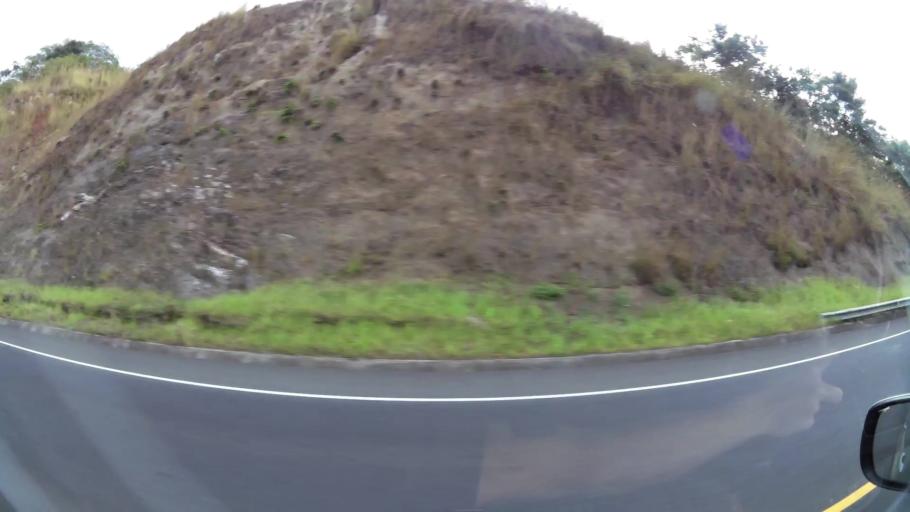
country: CR
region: Alajuela
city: Atenas
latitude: 9.9480
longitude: -84.3637
